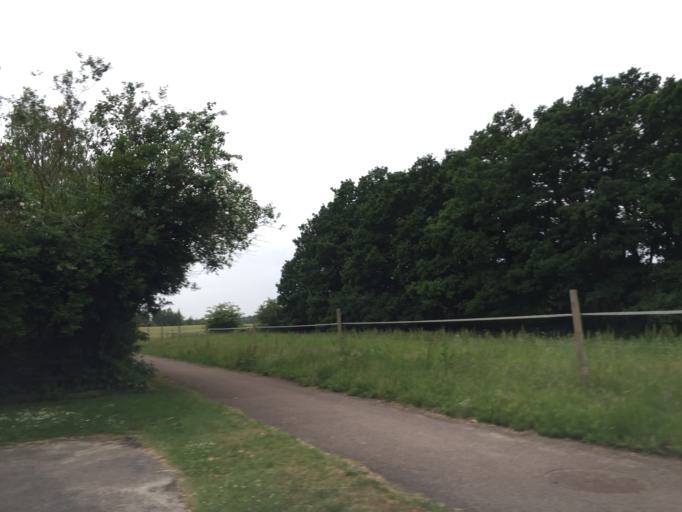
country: DK
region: Capital Region
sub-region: Lyngby-Tarbaek Kommune
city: Kongens Lyngby
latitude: 55.7742
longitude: 12.5264
